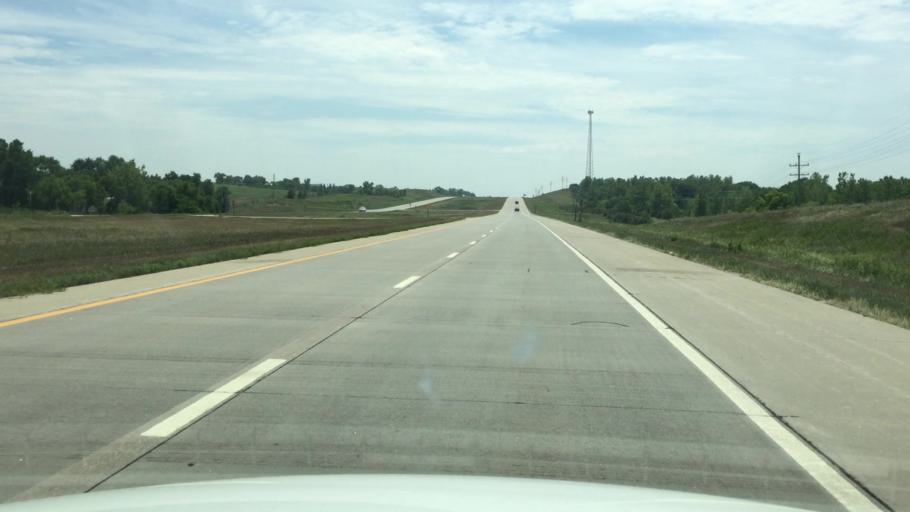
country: US
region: Kansas
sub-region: Shawnee County
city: Silver Lake
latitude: 39.2562
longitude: -95.7201
